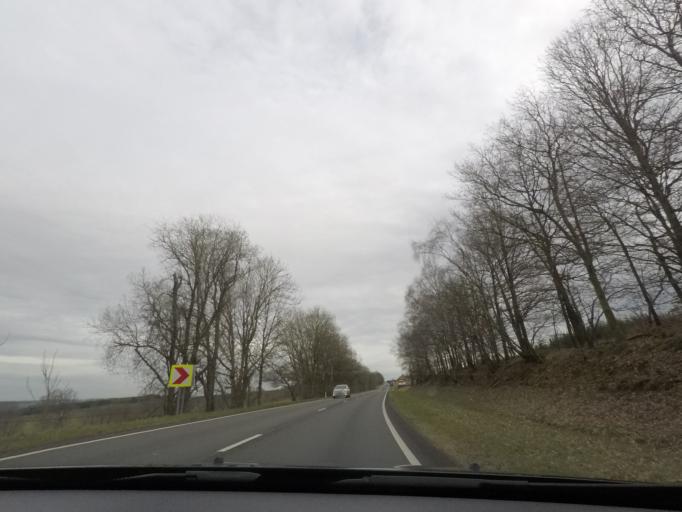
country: BE
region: Wallonia
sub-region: Province du Luxembourg
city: Bastogne
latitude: 49.9840
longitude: 5.7947
